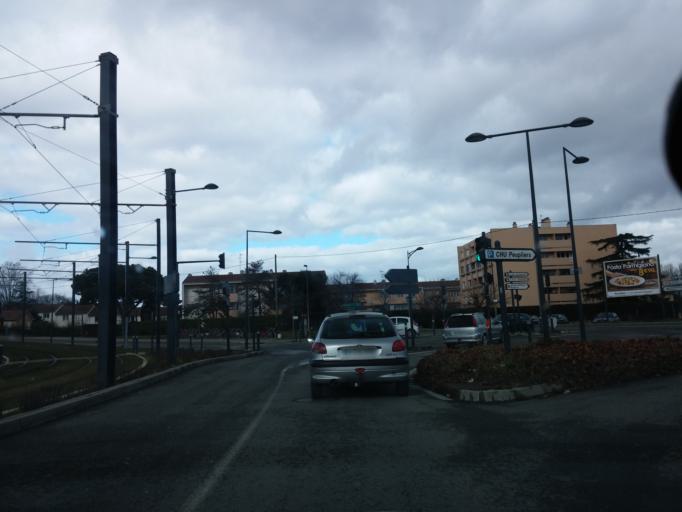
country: FR
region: Midi-Pyrenees
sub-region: Departement de la Haute-Garonne
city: Blagnac
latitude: 43.6131
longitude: 1.4014
